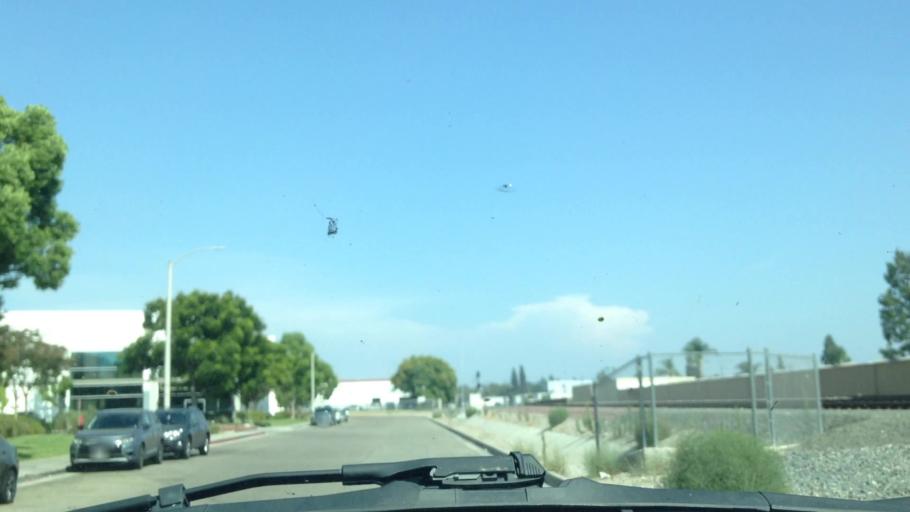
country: US
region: California
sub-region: Orange County
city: Buena Park
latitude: 33.8723
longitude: -117.9676
